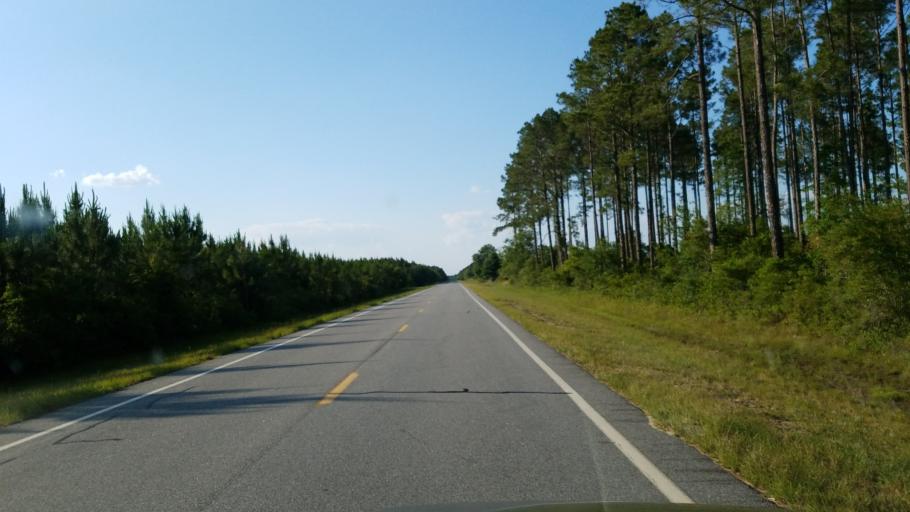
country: US
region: Georgia
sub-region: Echols County
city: Statenville
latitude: 30.8632
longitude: -83.0517
